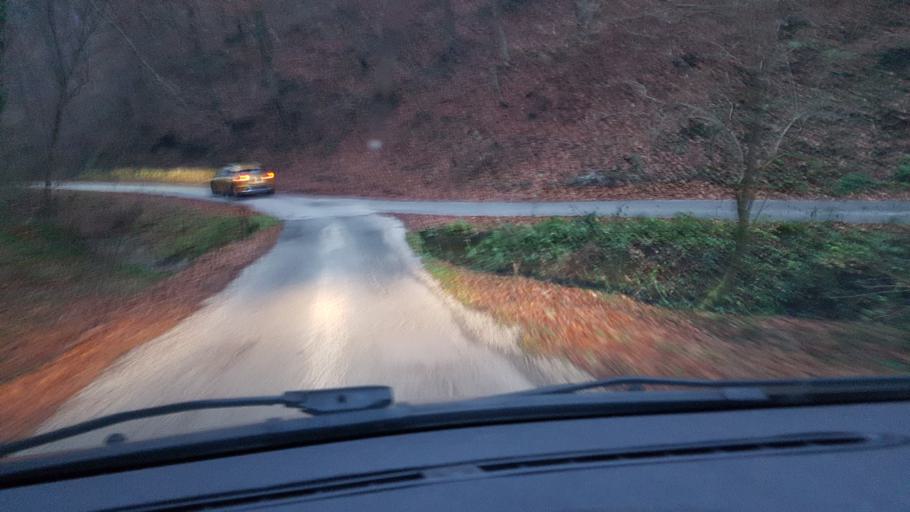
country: HR
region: Krapinsko-Zagorska
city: Pregrada
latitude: 46.1925
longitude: 15.7388
